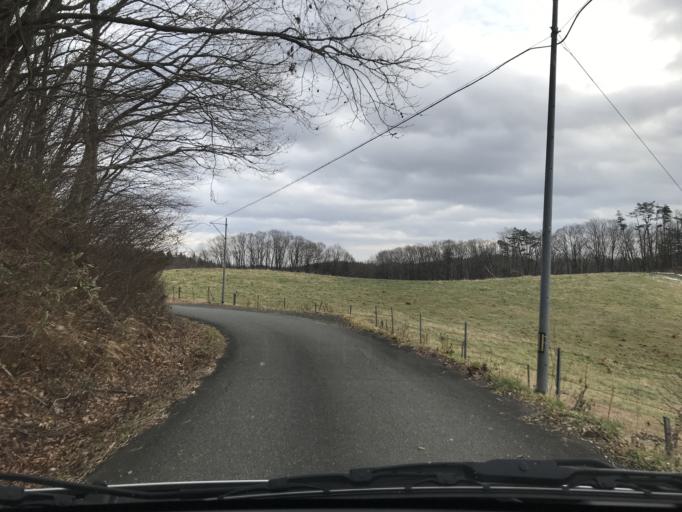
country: JP
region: Iwate
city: Ichinoseki
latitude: 38.9768
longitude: 141.0223
